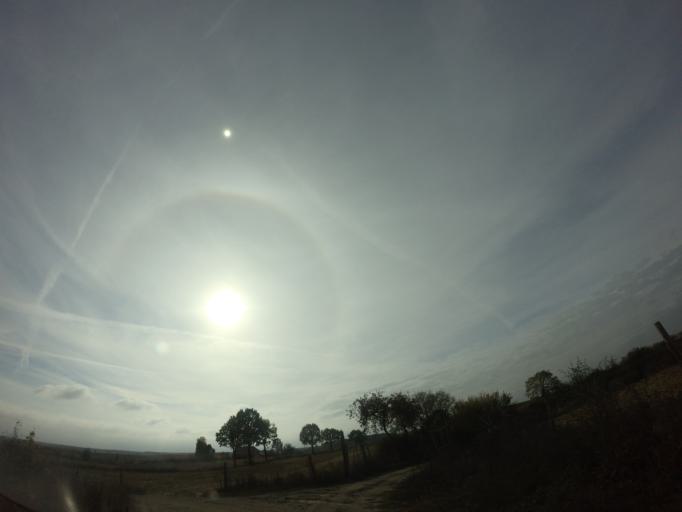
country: PL
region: West Pomeranian Voivodeship
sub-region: Powiat choszczenski
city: Drawno
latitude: 53.2378
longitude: 15.7288
